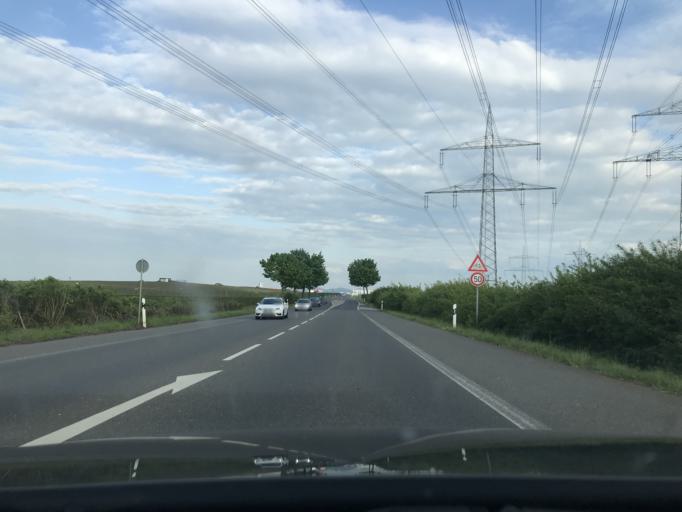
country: DE
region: North Rhine-Westphalia
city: Bornheim
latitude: 50.7644
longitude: 7.0137
